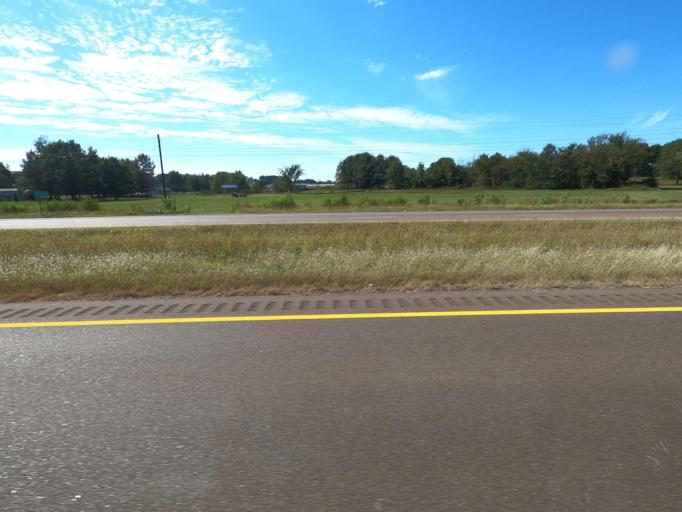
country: US
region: Tennessee
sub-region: Lauderdale County
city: Halls
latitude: 35.9244
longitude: -89.2798
